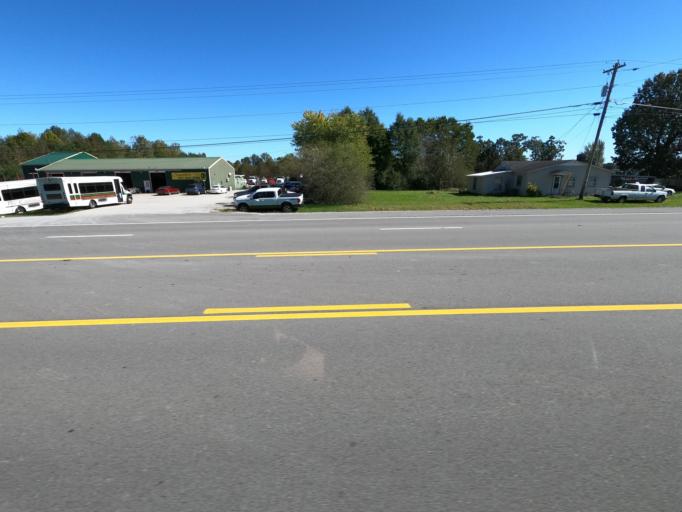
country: US
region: Tennessee
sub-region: Maury County
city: Mount Pleasant
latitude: 35.4332
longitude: -87.2807
